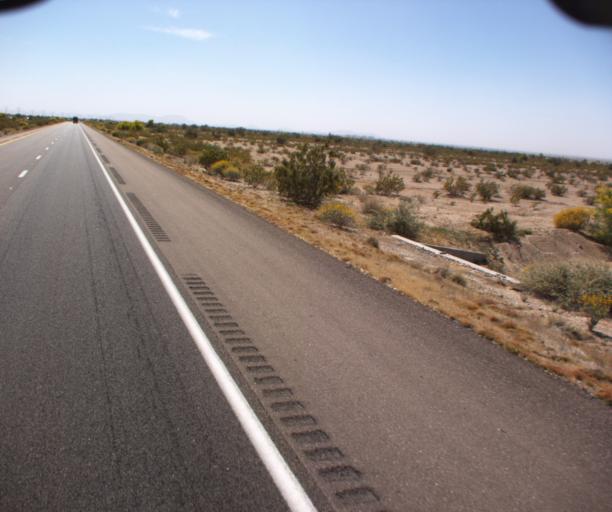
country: US
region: Arizona
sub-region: Maricopa County
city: Gila Bend
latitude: 33.0264
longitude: -112.6488
